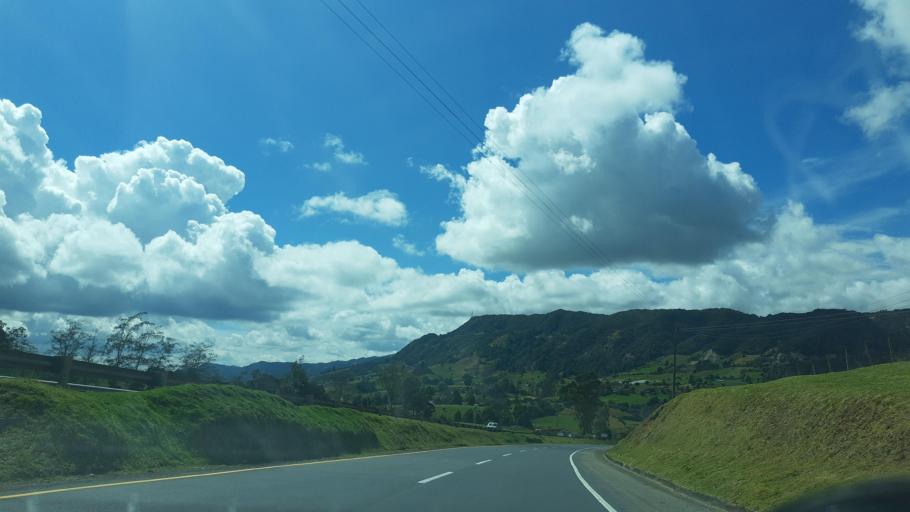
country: CO
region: Boyaca
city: Ventaquemada
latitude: 5.3975
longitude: -73.4868
